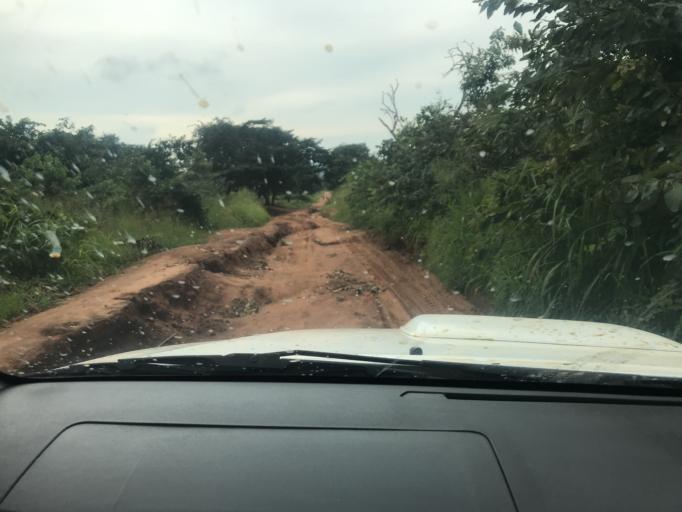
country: TZ
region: Mtwara
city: Newala Kisimani
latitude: -11.3784
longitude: 39.3508
